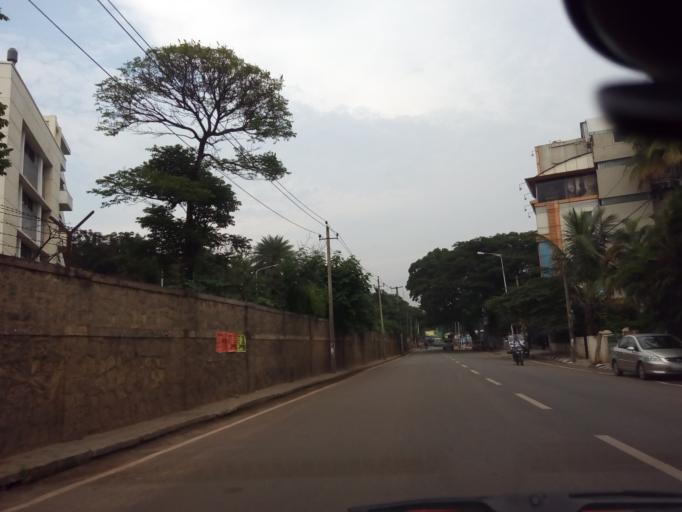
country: IN
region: Karnataka
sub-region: Bangalore Urban
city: Bangalore
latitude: 13.0239
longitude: 77.5628
